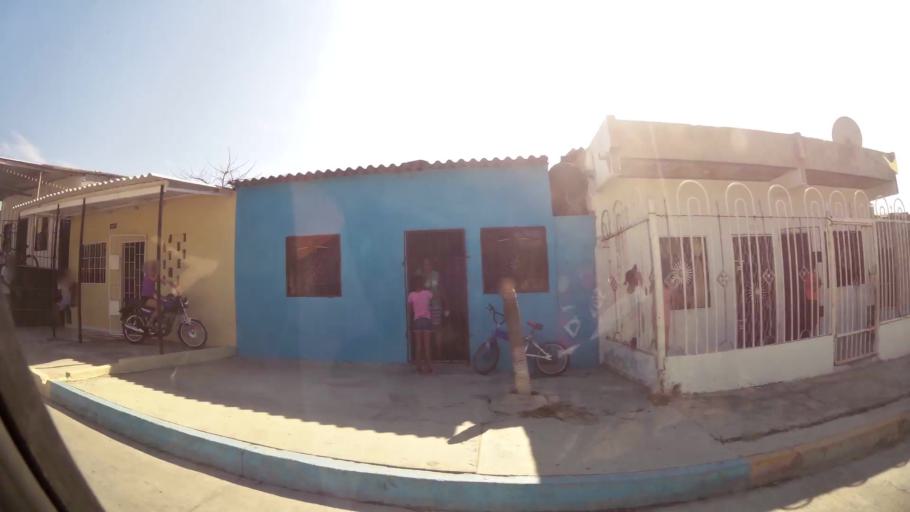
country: CO
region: Atlantico
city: Barranquilla
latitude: 10.9311
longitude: -74.8218
